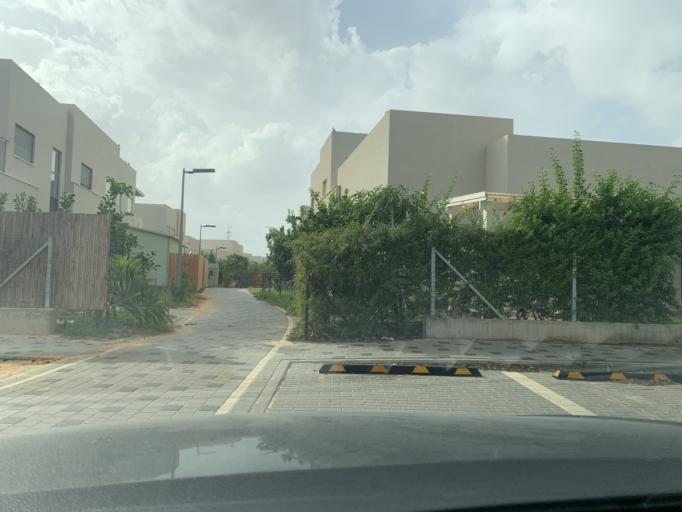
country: IL
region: Central District
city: Tirah
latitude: 32.2162
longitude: 34.9349
